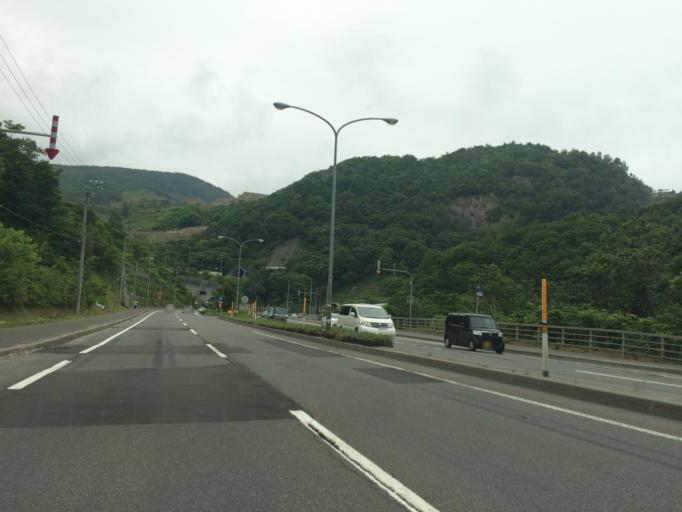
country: JP
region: Hokkaido
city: Otaru
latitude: 43.1624
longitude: 141.1025
